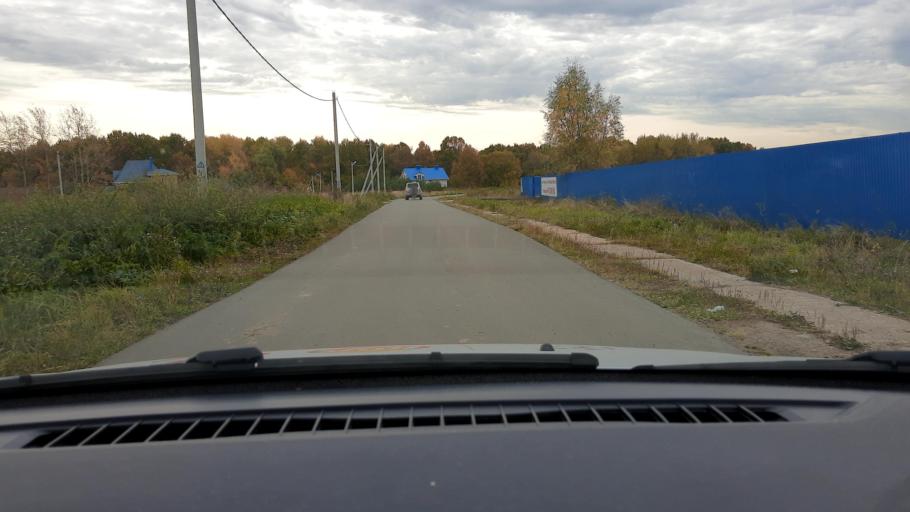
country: RU
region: Nizjnij Novgorod
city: Babino
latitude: 56.1293
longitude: 43.6473
